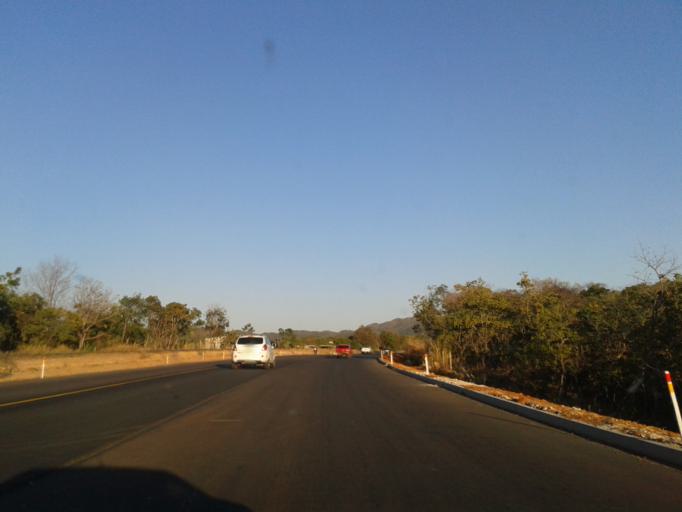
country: BR
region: Goias
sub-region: Goias
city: Goias
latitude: -15.9689
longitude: -50.1103
